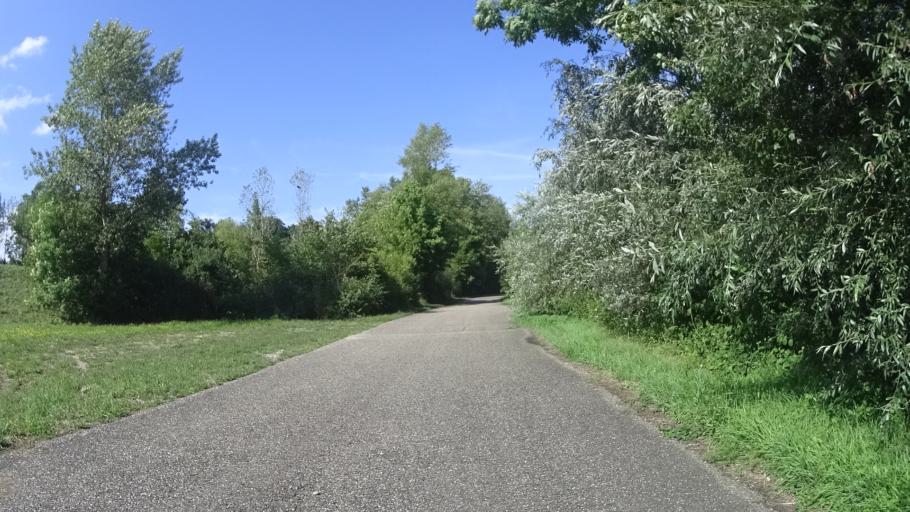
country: DE
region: Baden-Wuerttemberg
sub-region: Karlsruhe Region
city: Hugelsheim
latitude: 48.8373
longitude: 8.1030
